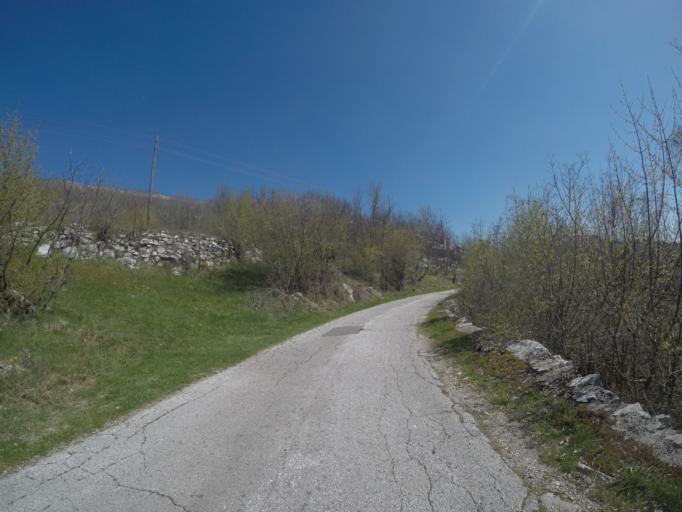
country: ME
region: Cetinje
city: Cetinje
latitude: 42.5287
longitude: 18.9686
